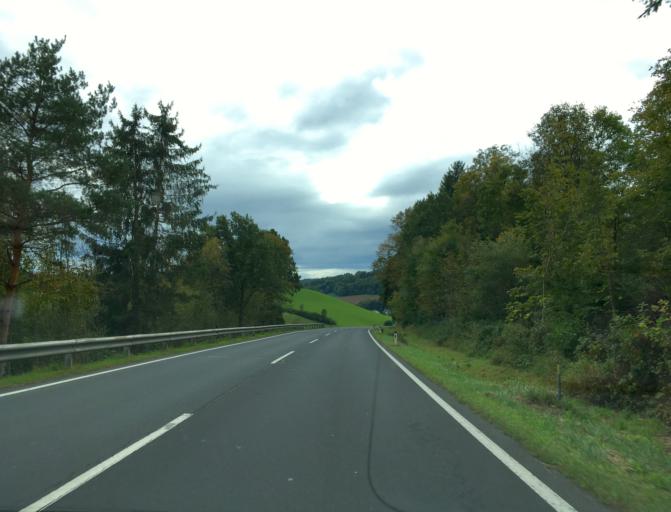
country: AT
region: Lower Austria
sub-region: Politischer Bezirk Wiener Neustadt
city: Bad Schonau
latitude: 47.5109
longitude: 16.2015
